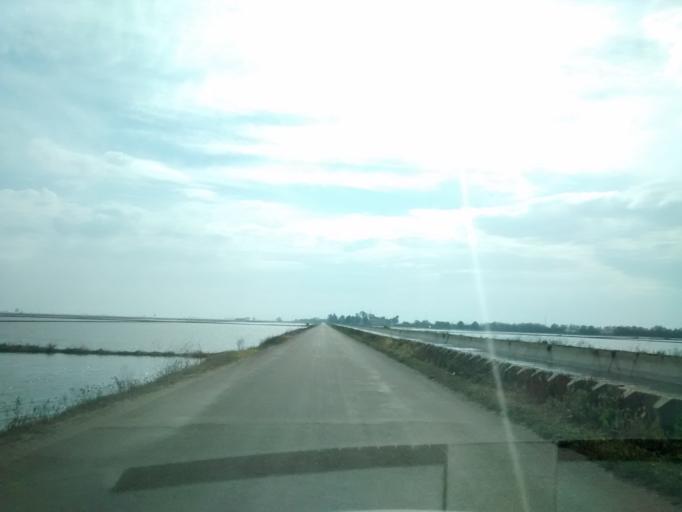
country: ES
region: Catalonia
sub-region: Provincia de Tarragona
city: Deltebre
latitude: 40.7028
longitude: 0.8216
